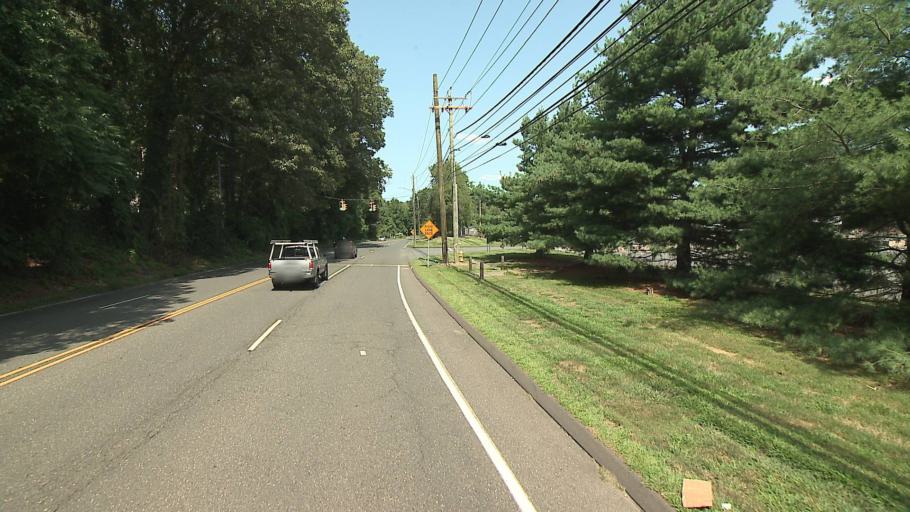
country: US
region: Connecticut
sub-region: New Haven County
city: City of Milford (balance)
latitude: 41.2561
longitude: -73.0994
